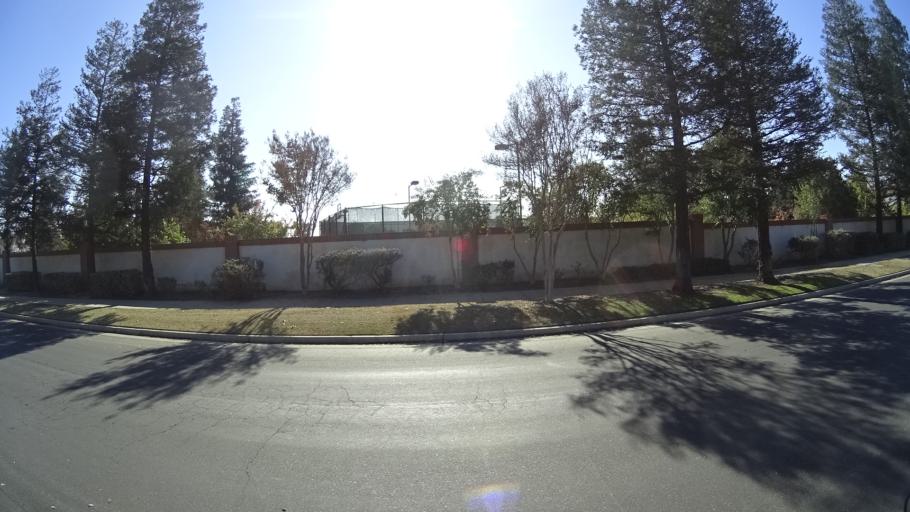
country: US
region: California
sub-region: Kern County
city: Greenacres
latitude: 35.3286
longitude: -119.1221
